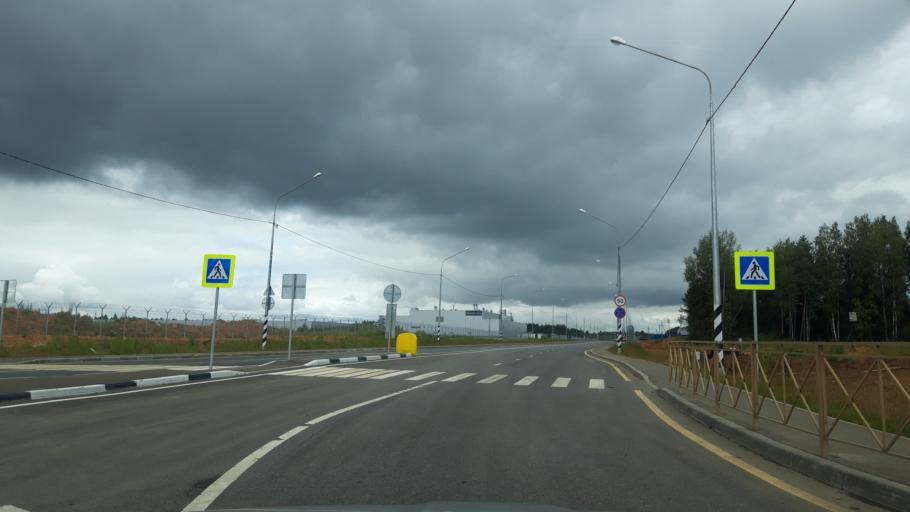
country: RU
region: Moskovskaya
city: Lozhki
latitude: 56.0803
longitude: 37.0913
